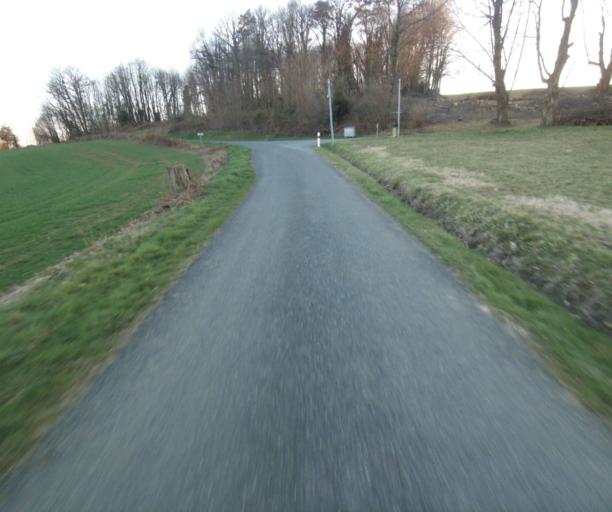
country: FR
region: Limousin
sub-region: Departement de la Correze
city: Uzerche
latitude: 45.3823
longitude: 1.6030
